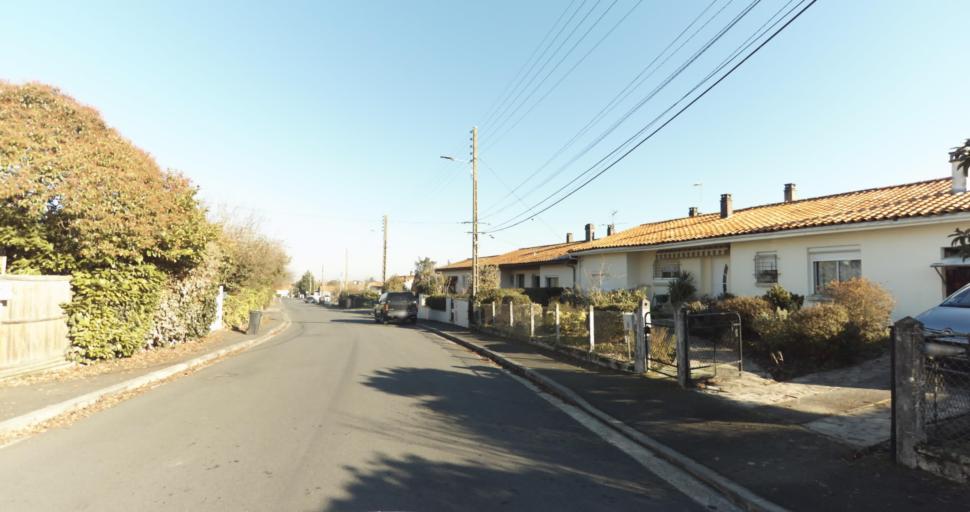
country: FR
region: Aquitaine
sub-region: Departement de la Gironde
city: Bassens
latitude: 44.8920
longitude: -0.5137
